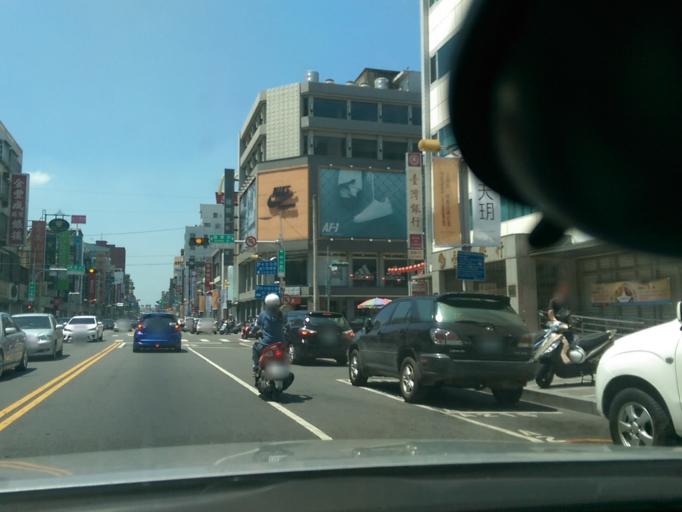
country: TW
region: Taiwan
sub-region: Chiayi
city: Jiayi Shi
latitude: 23.4798
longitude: 120.4490
